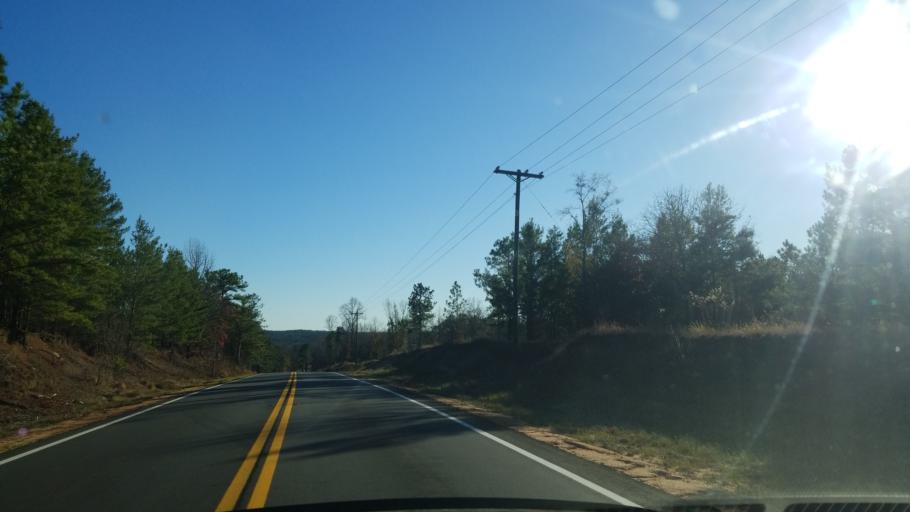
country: US
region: Georgia
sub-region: Talbot County
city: Talbotton
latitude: 32.5687
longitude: -84.5421
